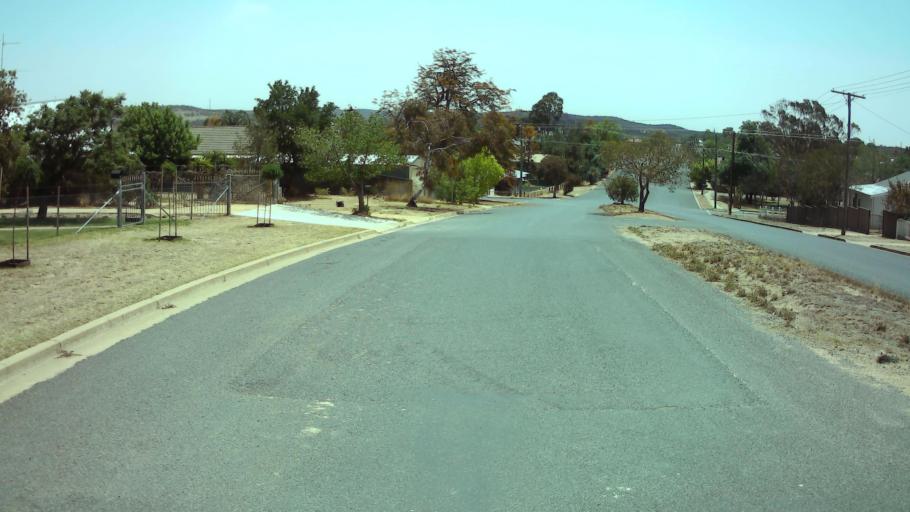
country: AU
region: New South Wales
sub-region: Weddin
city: Grenfell
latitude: -33.9018
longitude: 148.1590
